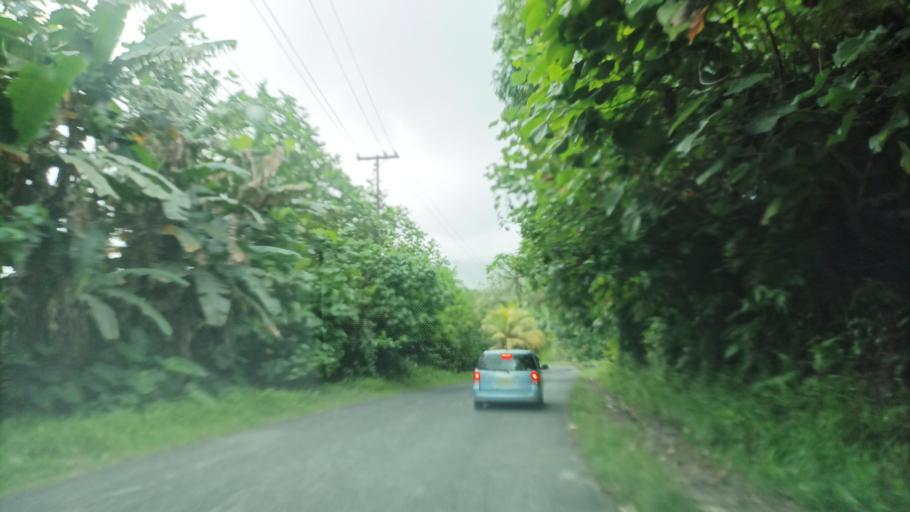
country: FM
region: Pohnpei
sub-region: Kolonia Municipality
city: Kolonia
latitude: 6.9540
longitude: 158.2238
